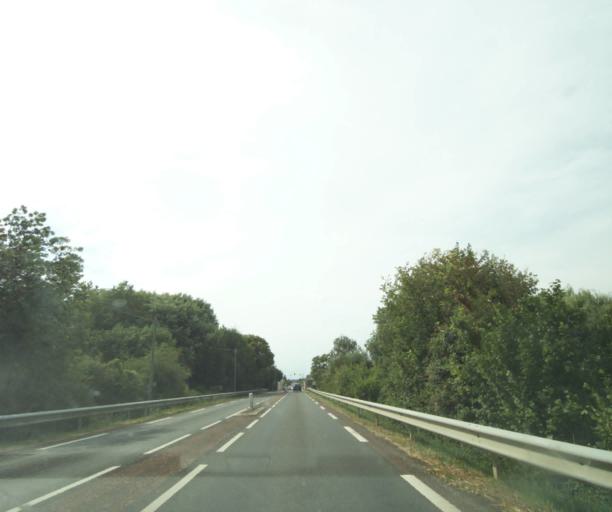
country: FR
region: Centre
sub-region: Departement d'Indre-et-Loire
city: Saint-Christophe-sur-le-Nais
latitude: 47.6634
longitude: 0.4743
